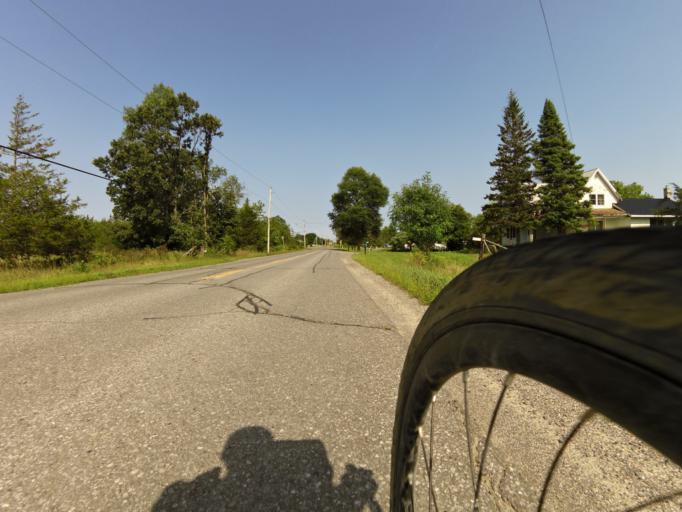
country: CA
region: Ontario
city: Skatepark
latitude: 44.2476
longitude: -76.7228
